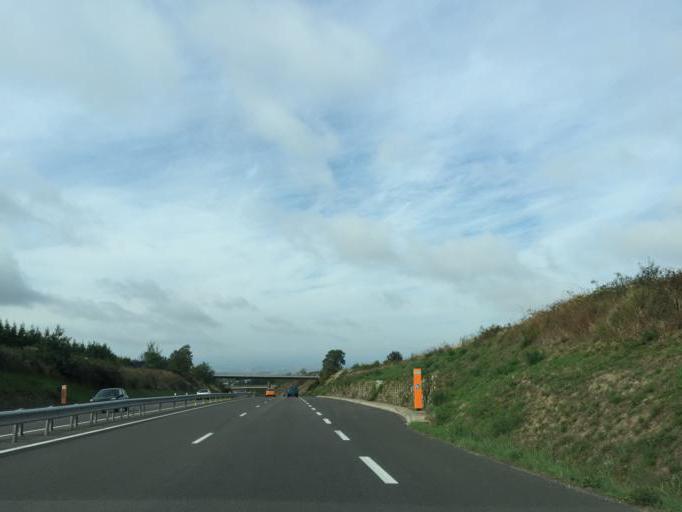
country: FR
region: Rhone-Alpes
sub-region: Departement de la Loire
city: Andrezieux-Boutheon
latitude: 45.5194
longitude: 4.2782
